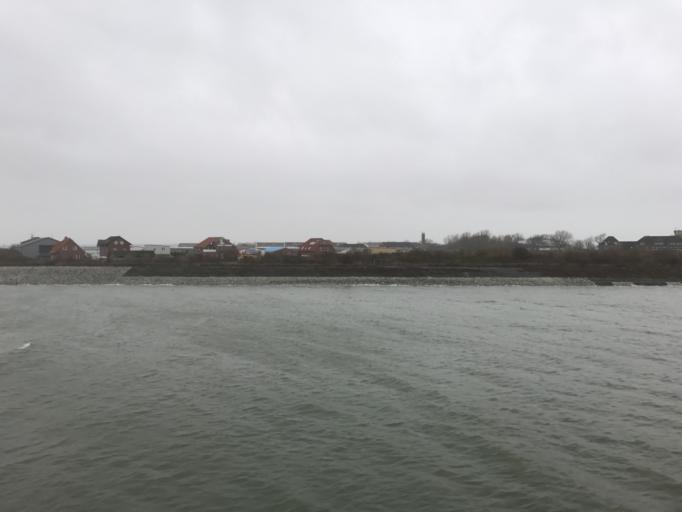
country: DE
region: Lower Saxony
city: Borkum
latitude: 53.5606
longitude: 6.7581
